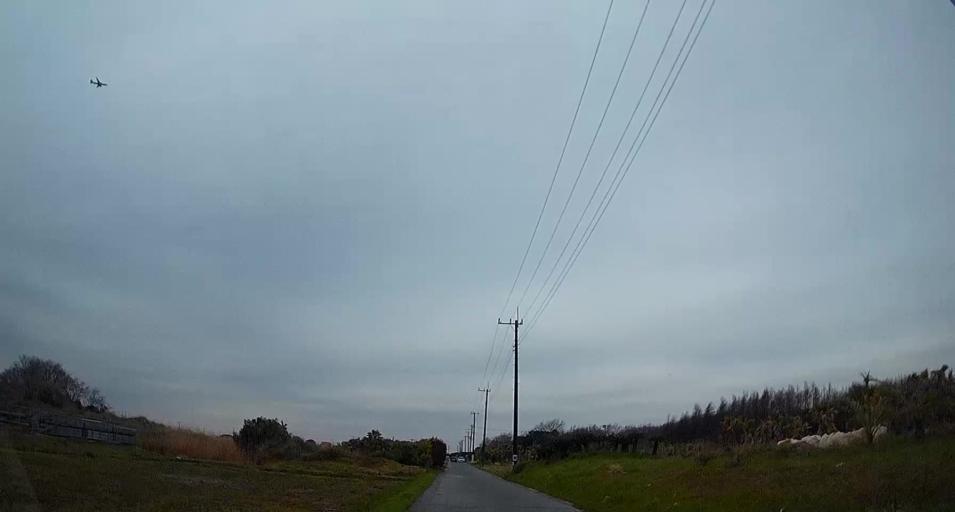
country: JP
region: Chiba
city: Kisarazu
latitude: 35.4133
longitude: 139.9147
